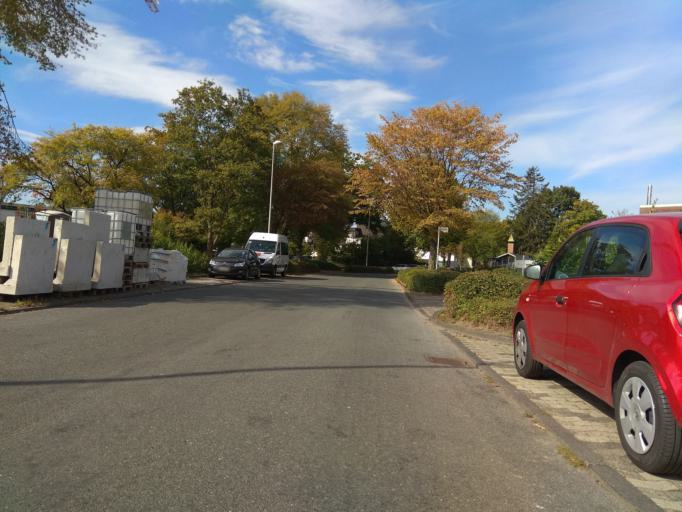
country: DE
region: North Rhine-Westphalia
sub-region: Regierungsbezirk Munster
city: Klein Reken
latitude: 51.7271
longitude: 7.0385
